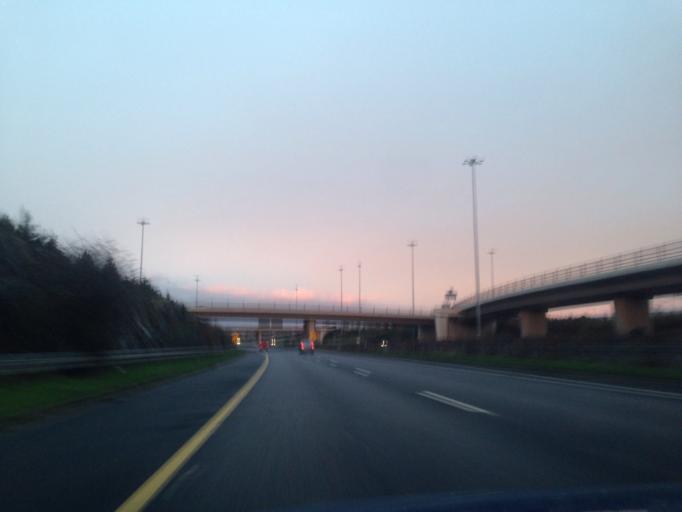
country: IE
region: Leinster
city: Sandyford
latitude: 53.2712
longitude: -6.2160
